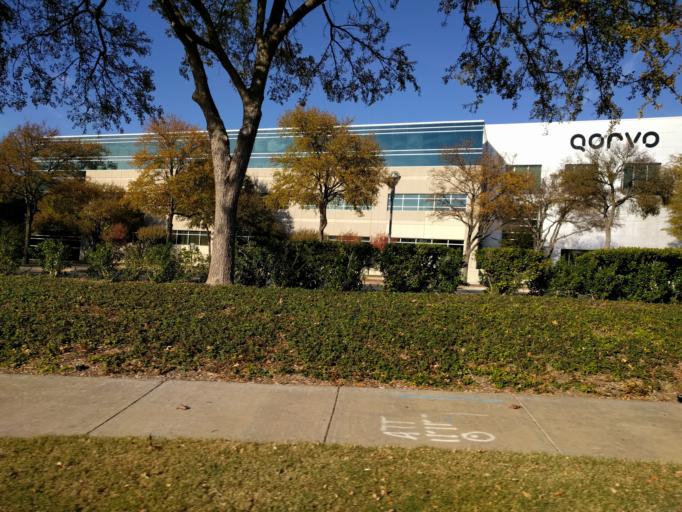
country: US
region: Texas
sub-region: Dallas County
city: Richardson
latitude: 32.9754
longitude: -96.7041
